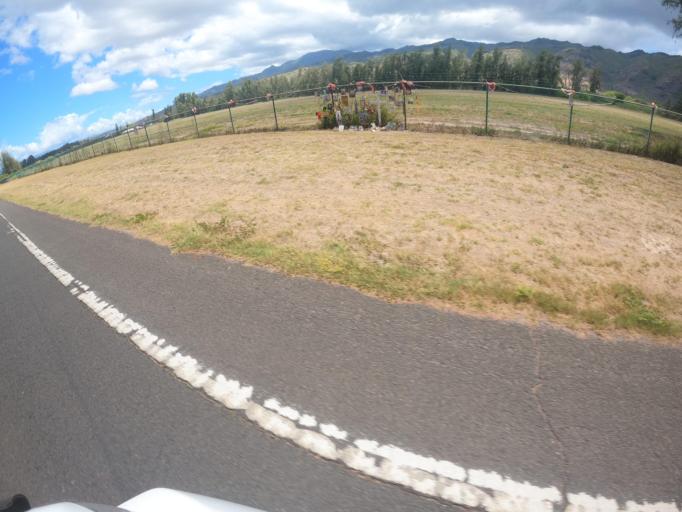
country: US
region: Hawaii
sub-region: Honolulu County
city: Mokuleia
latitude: 21.5811
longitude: -158.1886
